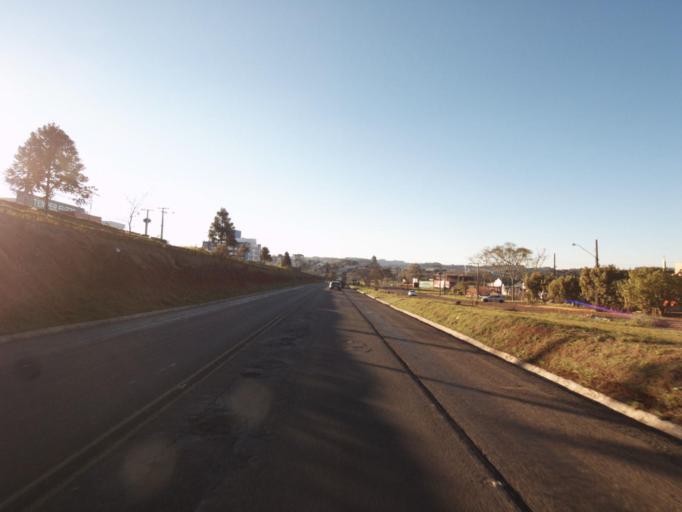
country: BR
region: Santa Catarina
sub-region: Chapeco
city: Chapeco
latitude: -26.8569
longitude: -52.9799
